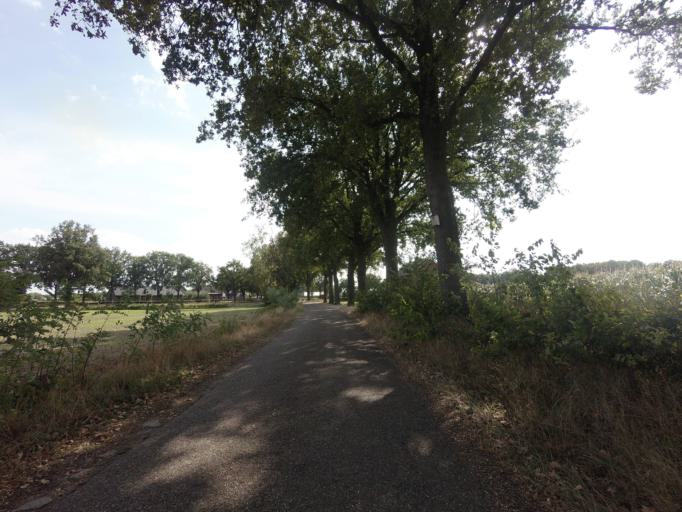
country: NL
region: North Brabant
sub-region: Gemeente Someren
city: Someren
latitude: 51.4139
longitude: 5.6756
